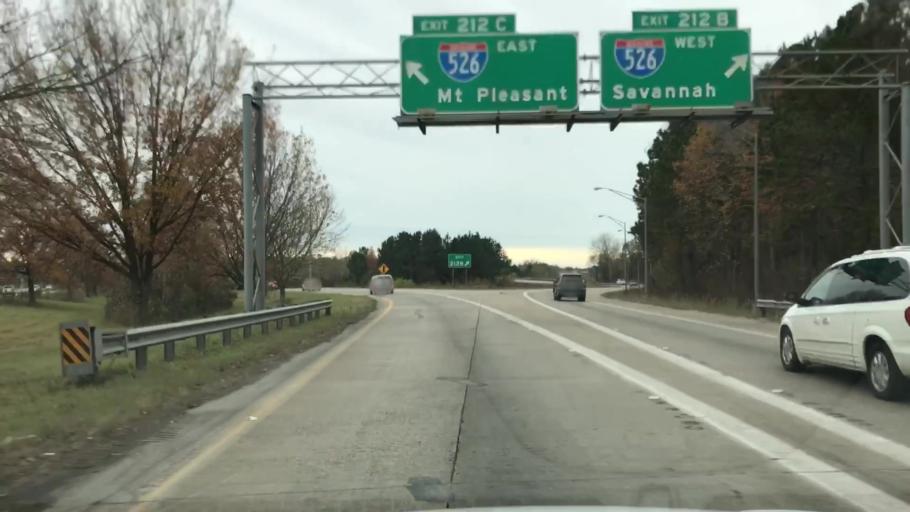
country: US
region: South Carolina
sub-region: Berkeley County
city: Hanahan
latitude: 32.8857
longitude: -80.0205
